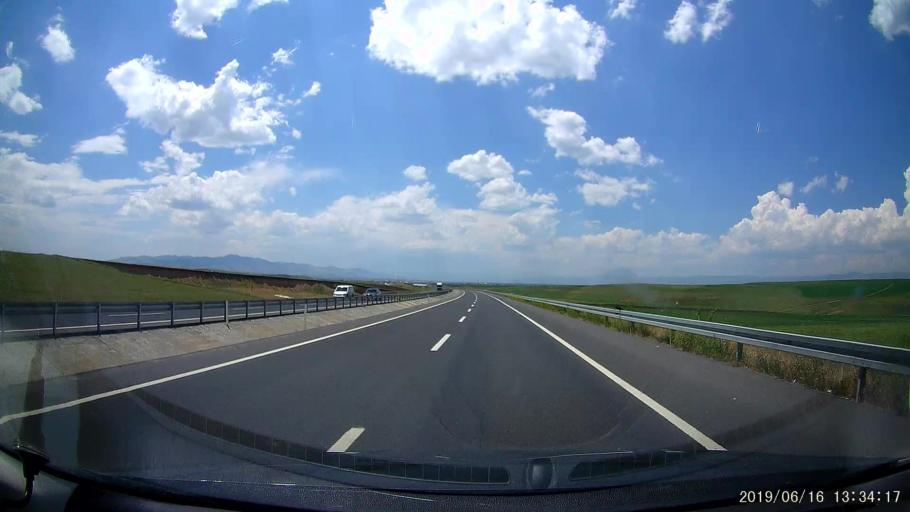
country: TR
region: Agri
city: Agri
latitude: 39.7123
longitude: 43.1309
